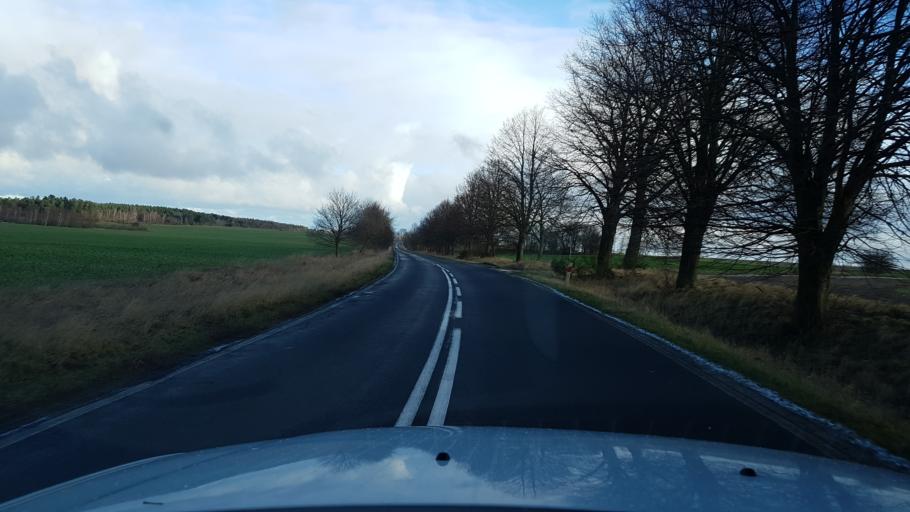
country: PL
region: West Pomeranian Voivodeship
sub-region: Powiat kolobrzeski
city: Grzybowo
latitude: 54.0776
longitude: 15.4421
